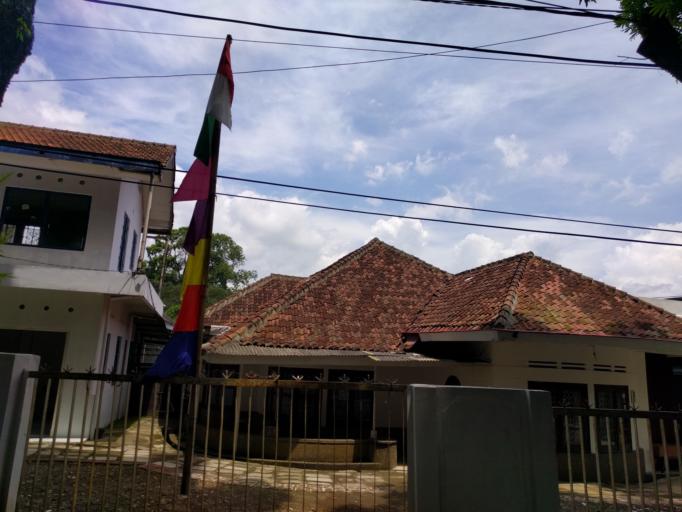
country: ID
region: West Java
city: Bogor
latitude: -6.5928
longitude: 106.8033
